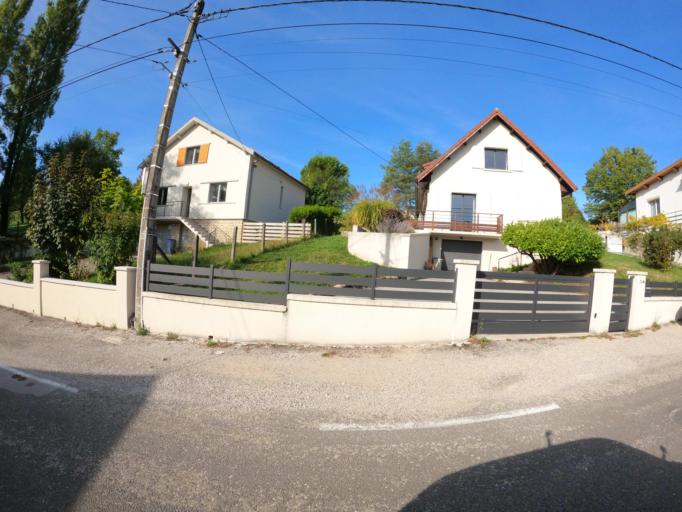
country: FR
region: Franche-Comte
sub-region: Departement du Jura
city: Montmorot
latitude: 46.6816
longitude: 5.5377
